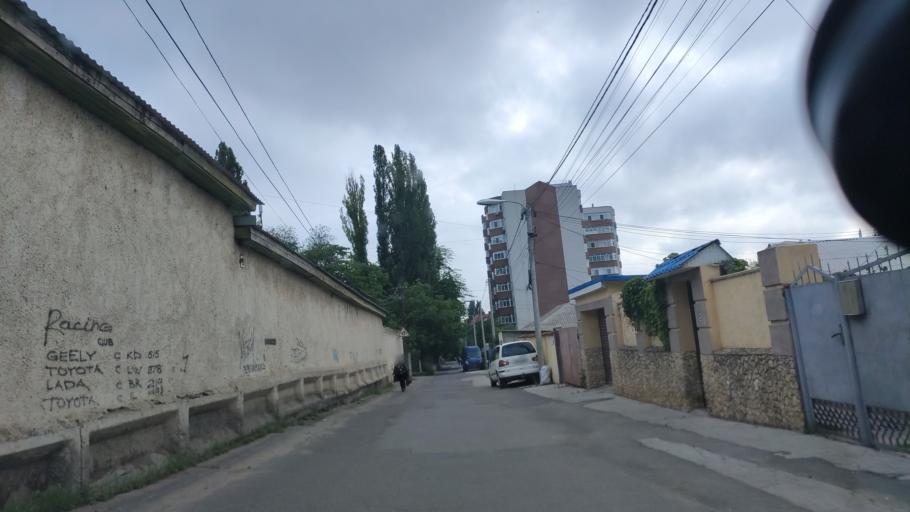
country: MD
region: Chisinau
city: Chisinau
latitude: 46.9841
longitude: 28.8707
